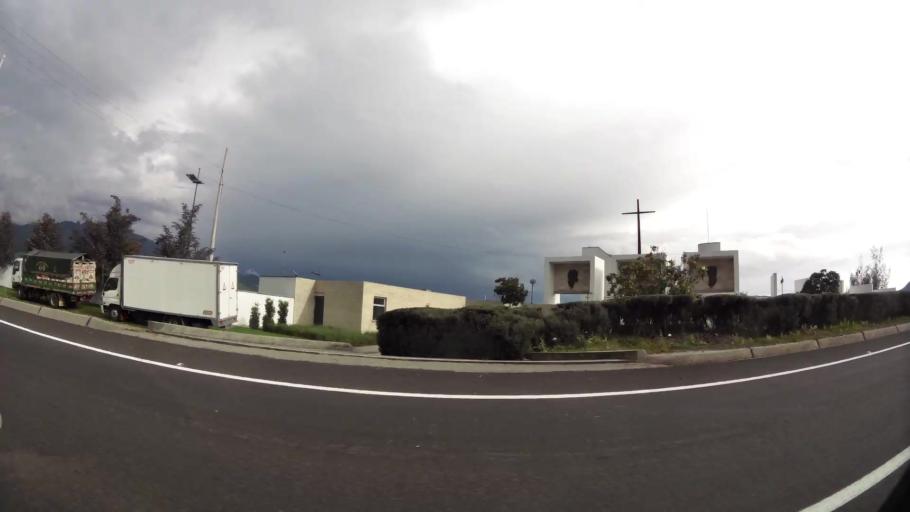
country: EC
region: Pichincha
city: Sangolqui
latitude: -0.3913
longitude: -78.5423
